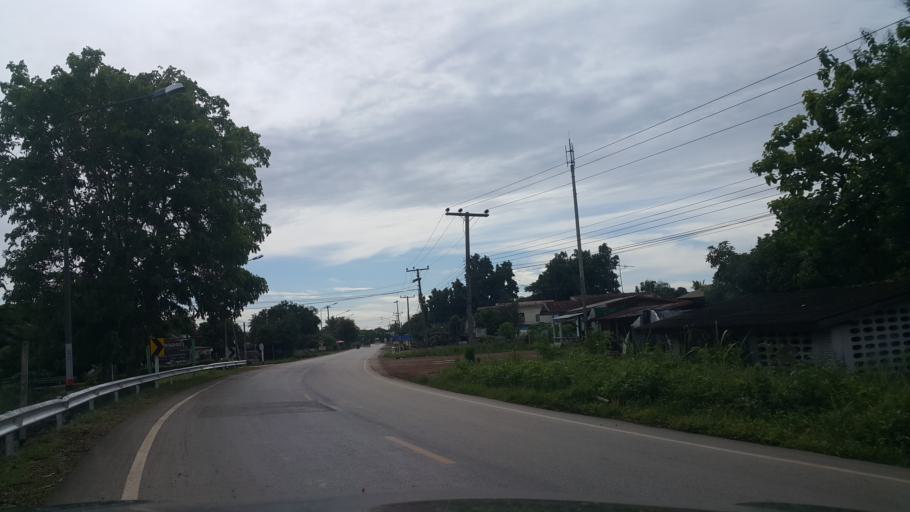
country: TH
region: Sukhothai
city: Si Nakhon
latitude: 17.2737
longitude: 99.9629
